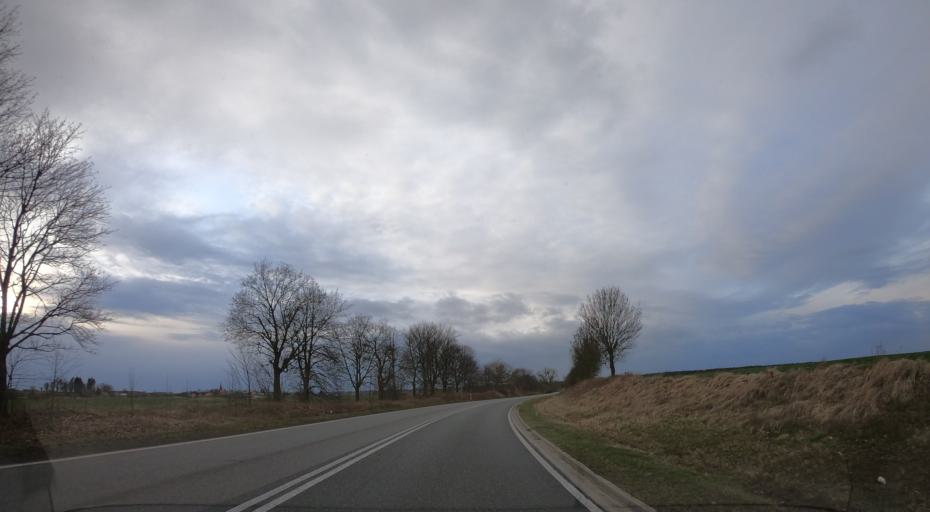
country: PL
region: West Pomeranian Voivodeship
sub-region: Powiat mysliborski
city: Nowogrodek Pomorski
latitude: 52.9049
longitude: 14.9741
